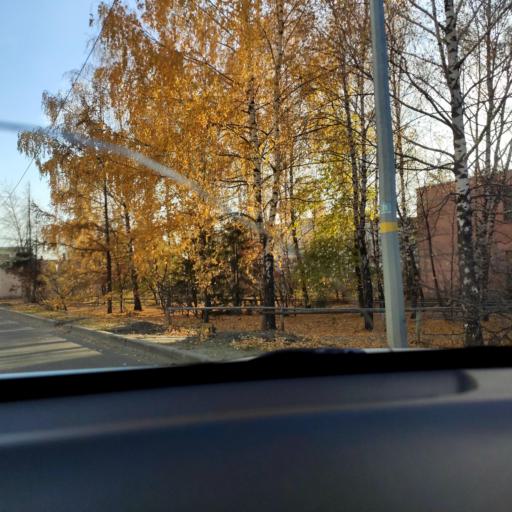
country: RU
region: Tatarstan
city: Staroye Arakchino
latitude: 55.8359
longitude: 49.0374
